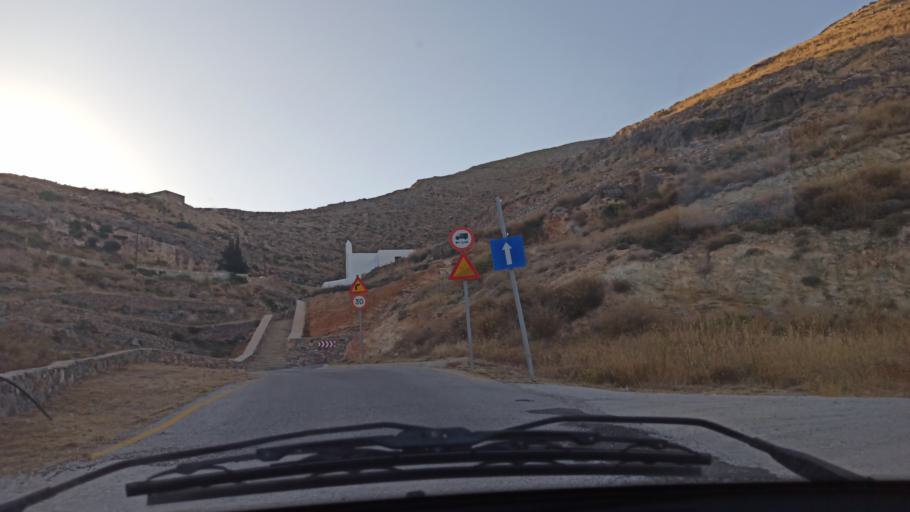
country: GR
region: South Aegean
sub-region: Nomos Kykladon
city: Ano Syros
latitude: 37.4534
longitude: 24.9364
